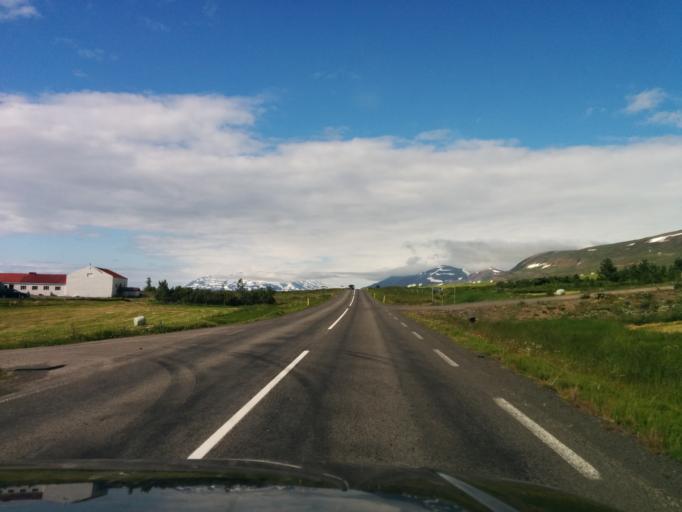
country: IS
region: Northeast
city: Akureyri
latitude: 65.7560
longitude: -18.0736
